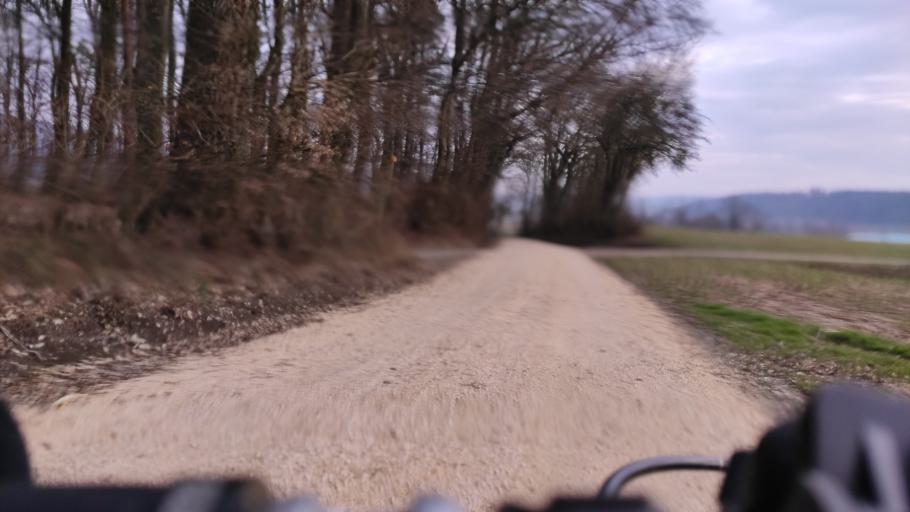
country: CH
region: Schaffhausen
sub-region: Bezirk Stein
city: Ramsen
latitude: 47.7171
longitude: 8.8049
